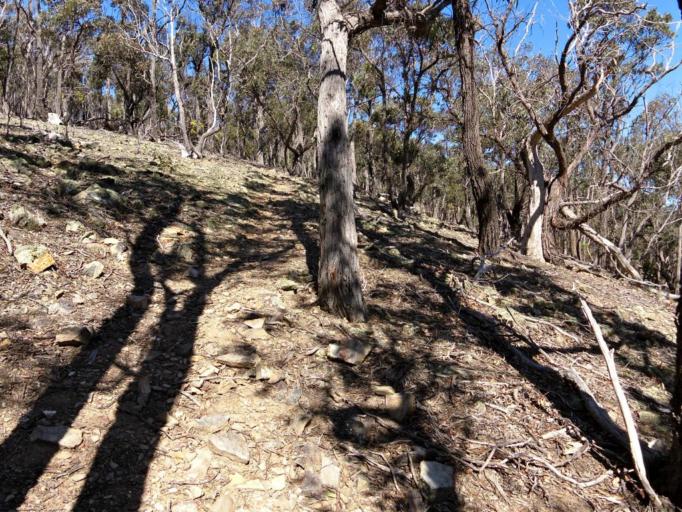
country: AU
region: Victoria
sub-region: Moorabool
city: Bacchus Marsh
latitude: -37.6672
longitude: 144.3212
